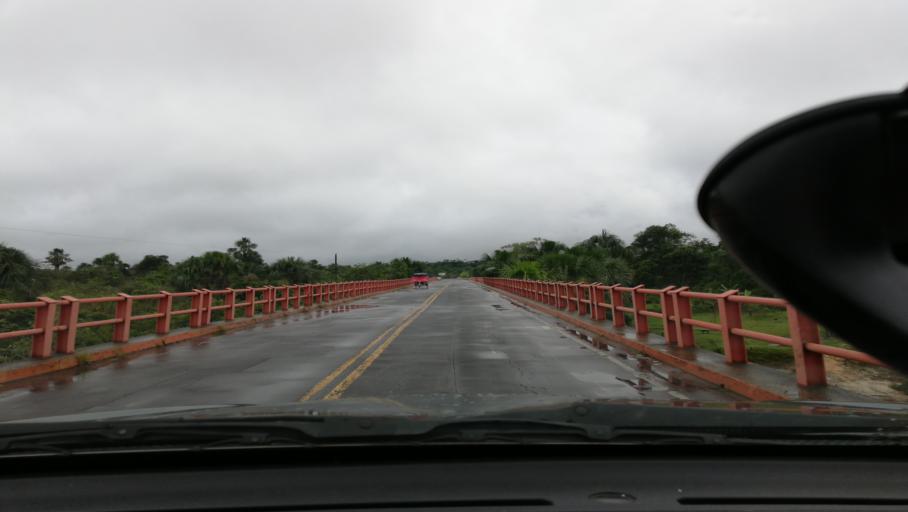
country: PE
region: Loreto
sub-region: Provincia de Loreto
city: Nauta
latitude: -4.2254
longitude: -73.4825
